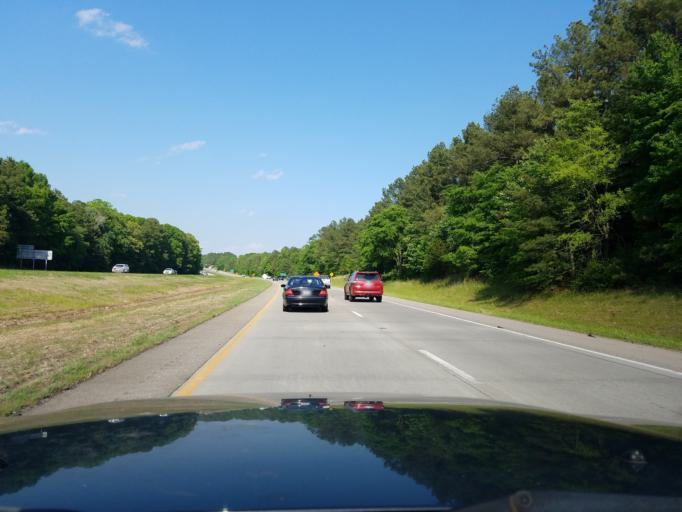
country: US
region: North Carolina
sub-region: Vance County
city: South Henderson
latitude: 36.3195
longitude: -78.4684
